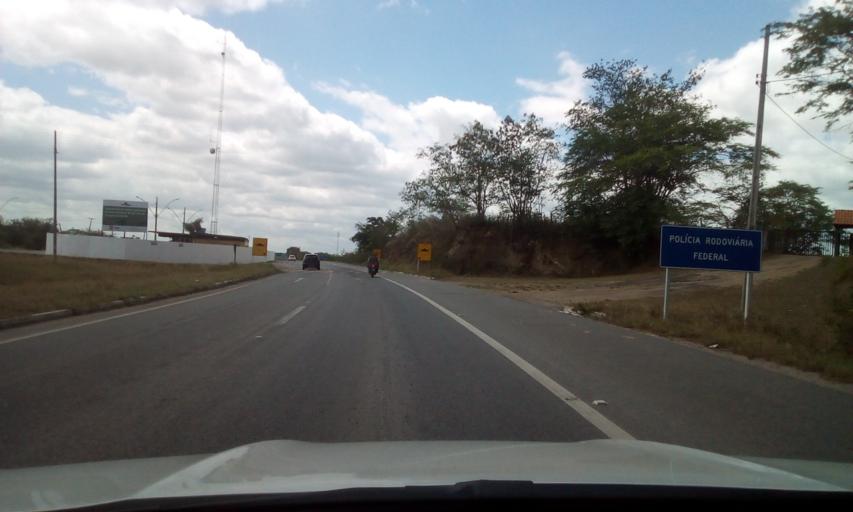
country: BR
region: Paraiba
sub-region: Campina Grande
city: Campina Grande
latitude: -7.2539
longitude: -35.8318
